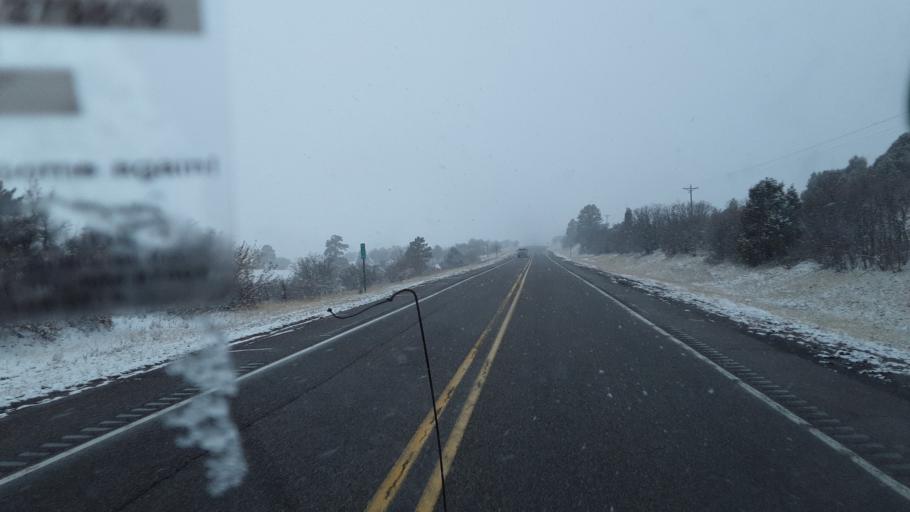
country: US
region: New Mexico
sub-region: Rio Arriba County
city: Chama
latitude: 36.8737
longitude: -106.6691
